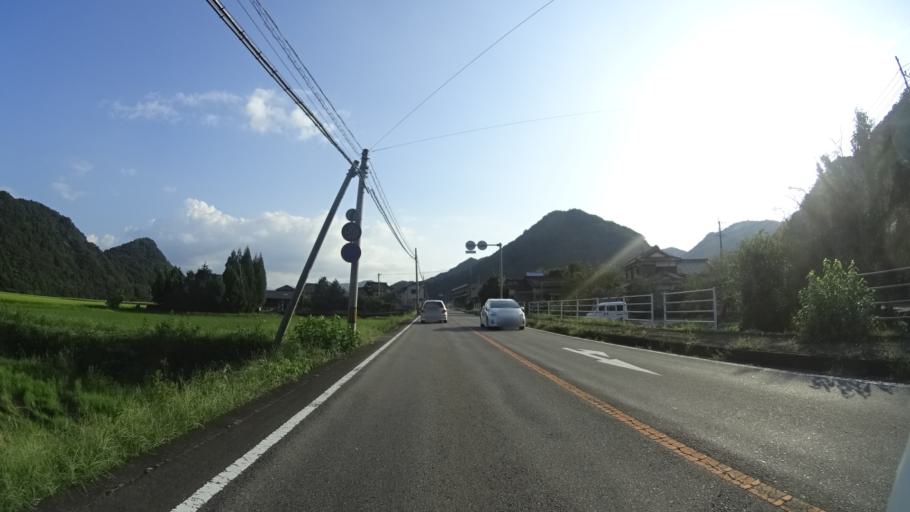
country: JP
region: Oita
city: Bungo-Takada-shi
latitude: 33.4761
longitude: 131.3305
